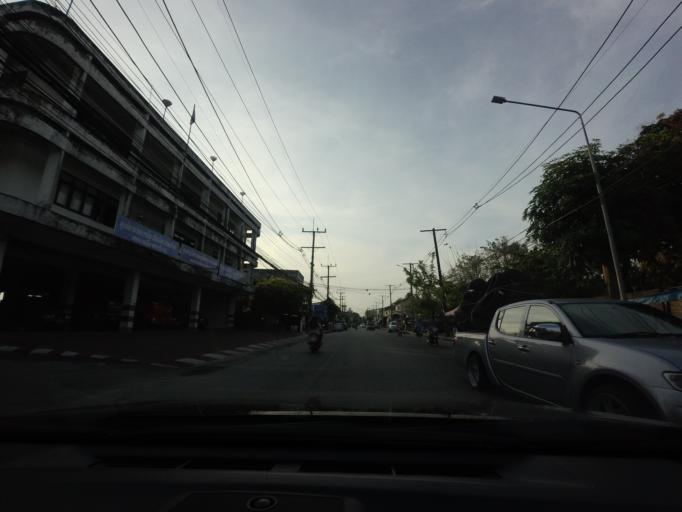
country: TH
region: Narathiwat
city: Narathiwat
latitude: 6.4232
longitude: 101.8289
